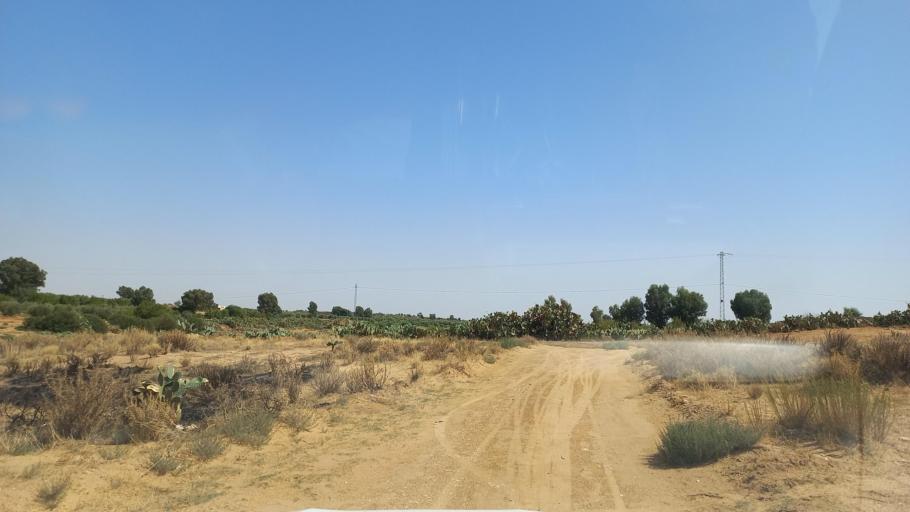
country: TN
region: Al Qasrayn
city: Kasserine
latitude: 35.2361
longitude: 9.0309
